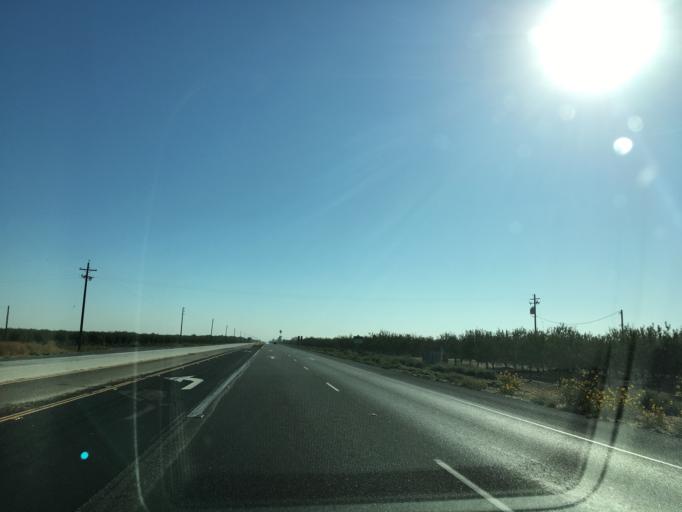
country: US
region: California
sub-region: Merced County
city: Dos Palos
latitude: 37.0835
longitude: -120.4570
